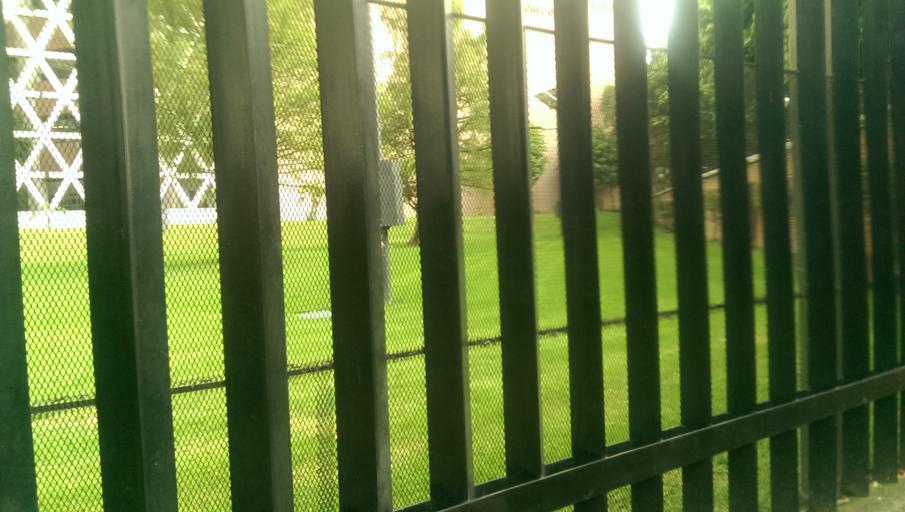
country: MX
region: Mexico City
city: Tlalpan
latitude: 19.2866
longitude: -99.1365
